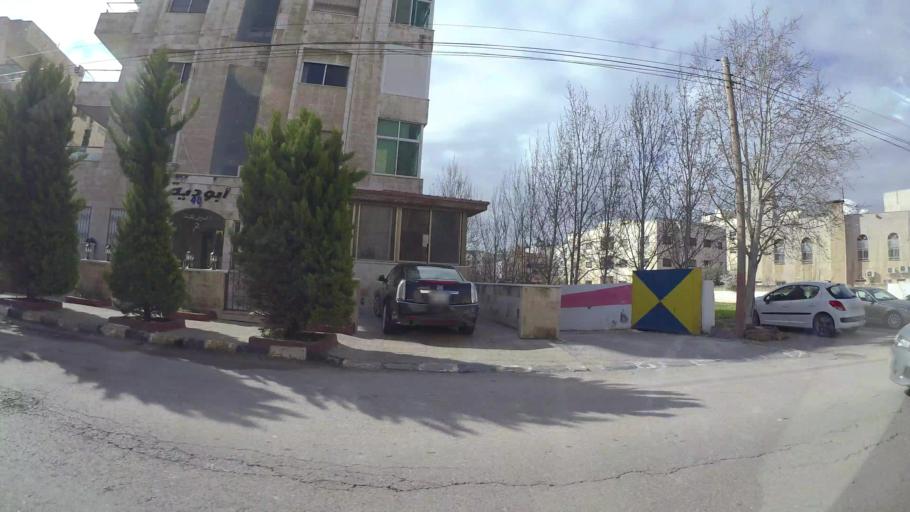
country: JO
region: Amman
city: Wadi as Sir
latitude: 31.9522
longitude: 35.8469
